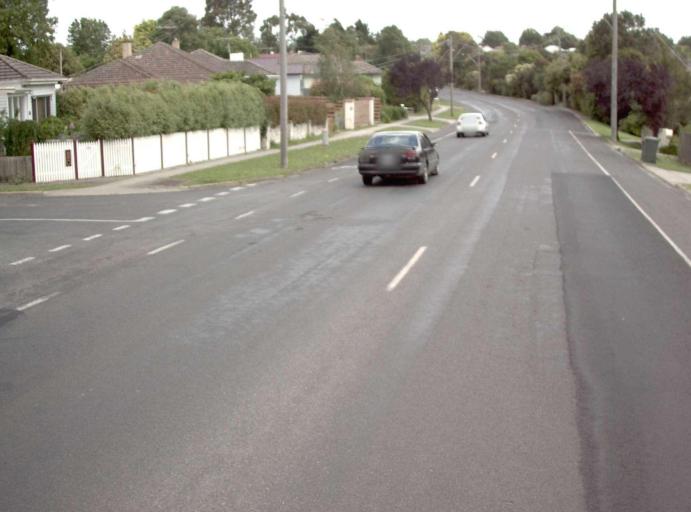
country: AU
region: Victoria
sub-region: Baw Baw
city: Warragul
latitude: -38.1497
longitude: 145.9359
